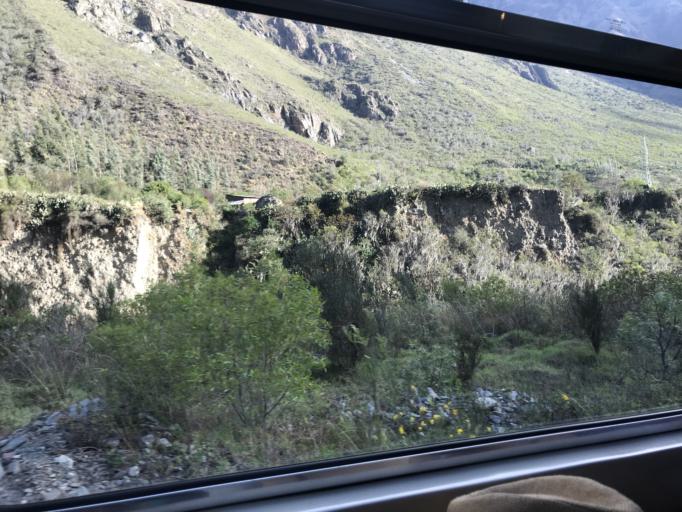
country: PE
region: Cusco
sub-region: Provincia de Urubamba
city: Ollantaytambo
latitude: -13.2196
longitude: -72.3903
